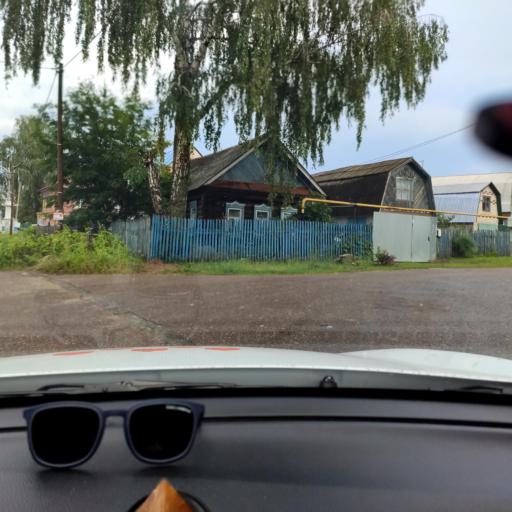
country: RU
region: Tatarstan
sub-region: Zelenodol'skiy Rayon
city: Vasil'yevo
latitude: 55.8298
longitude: 48.7079
